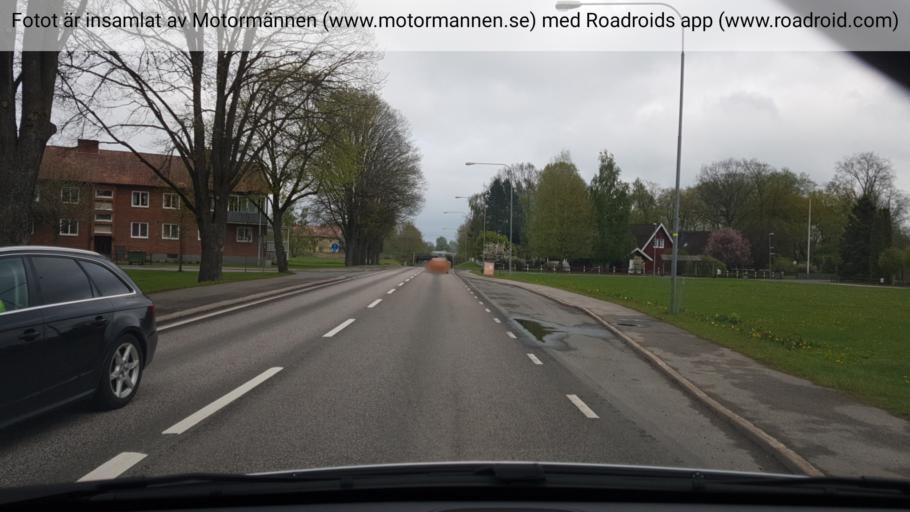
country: SE
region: Vaestra Goetaland
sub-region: Skovde Kommun
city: Stopen
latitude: 58.5709
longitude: 14.0051
